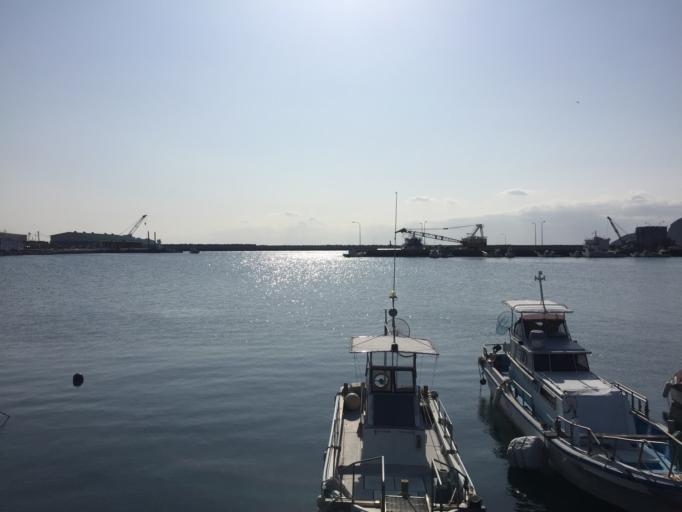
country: JP
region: Nagasaki
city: Togitsu
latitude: 32.8224
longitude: 129.7648
